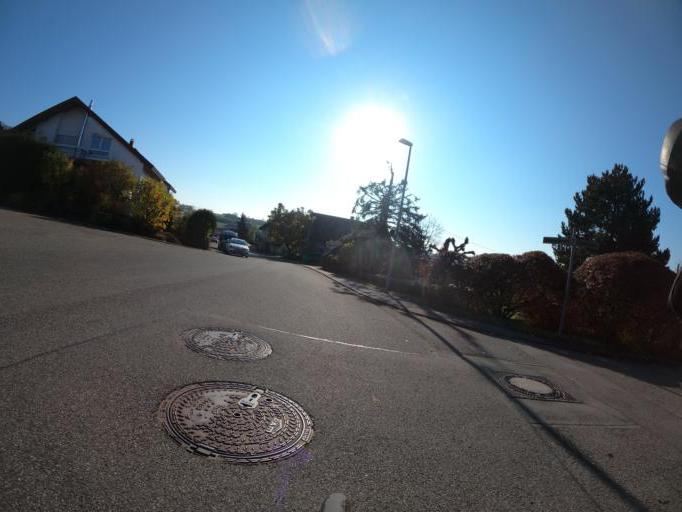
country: DE
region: Baden-Wuerttemberg
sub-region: Regierungsbezirk Stuttgart
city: Weil der Stadt
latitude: 48.7254
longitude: 8.8972
